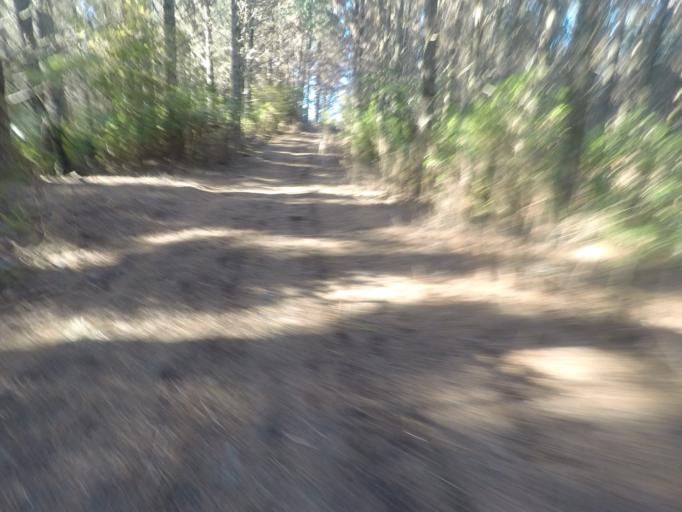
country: NZ
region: Auckland
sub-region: Auckland
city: Muriwai Beach
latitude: -36.7460
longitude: 174.5558
